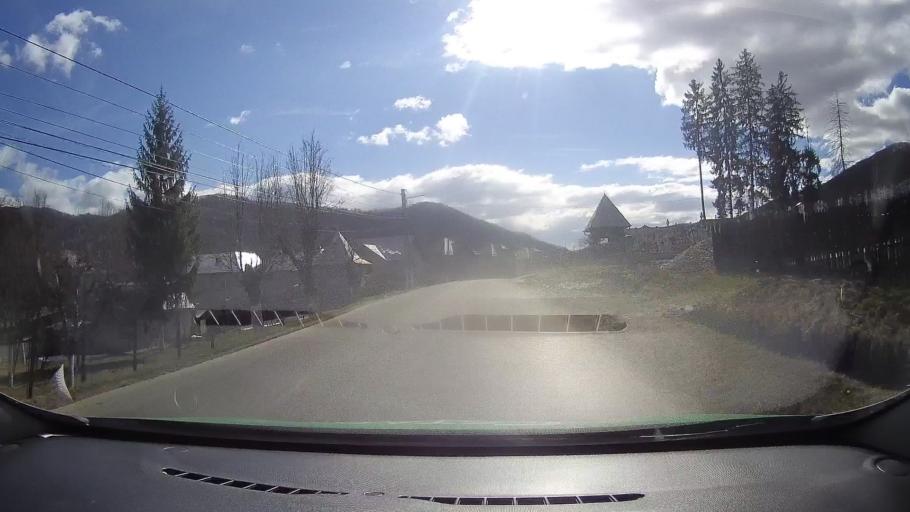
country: RO
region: Dambovita
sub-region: Comuna Vulcana Bai
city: Vulcana Bai
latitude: 45.0696
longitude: 25.3785
